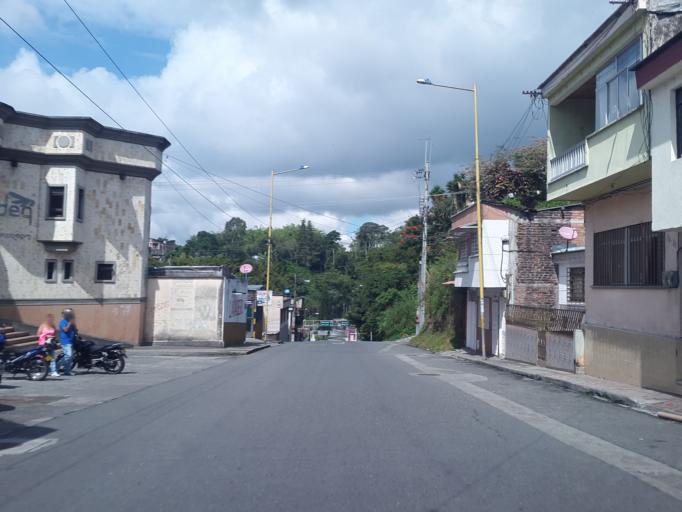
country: CO
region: Quindio
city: Calarca
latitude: 4.5320
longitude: -75.6434
